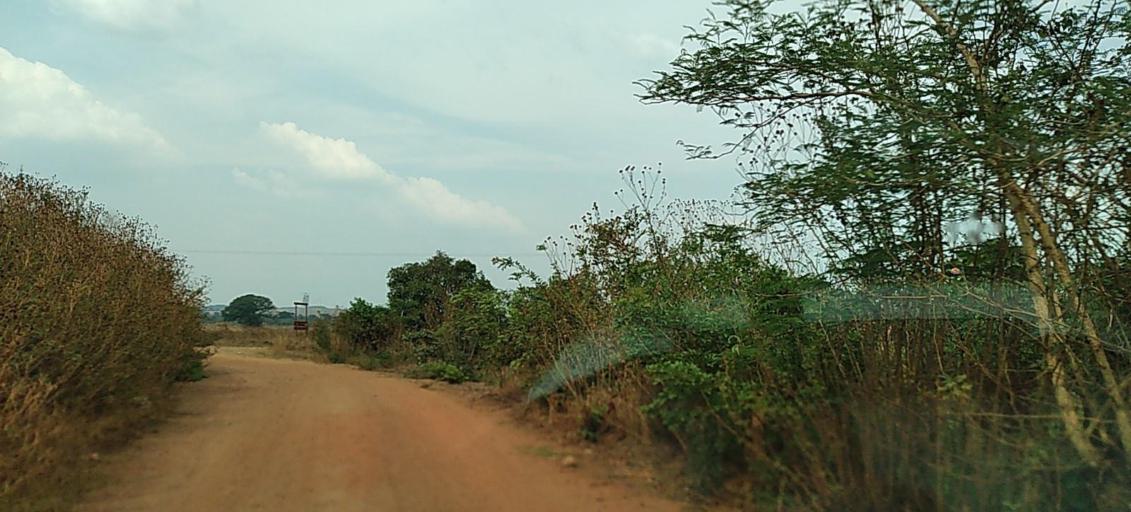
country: ZM
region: Copperbelt
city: Chililabombwe
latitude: -12.3941
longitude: 27.8055
